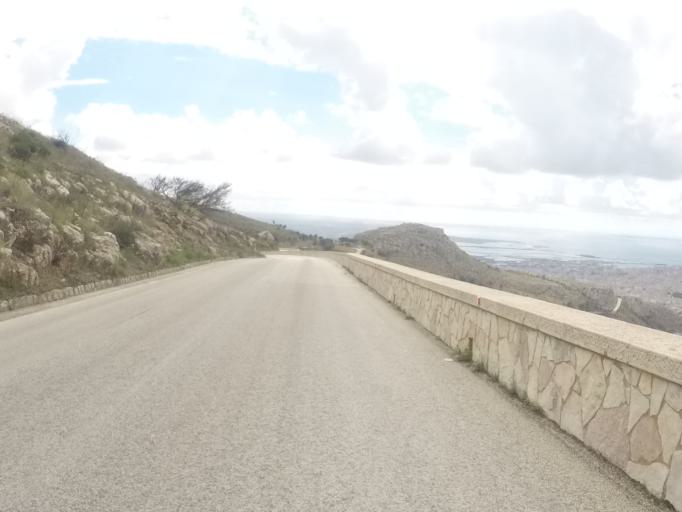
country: IT
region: Sicily
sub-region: Trapani
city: Casa Santa
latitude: 38.0430
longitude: 12.5666
